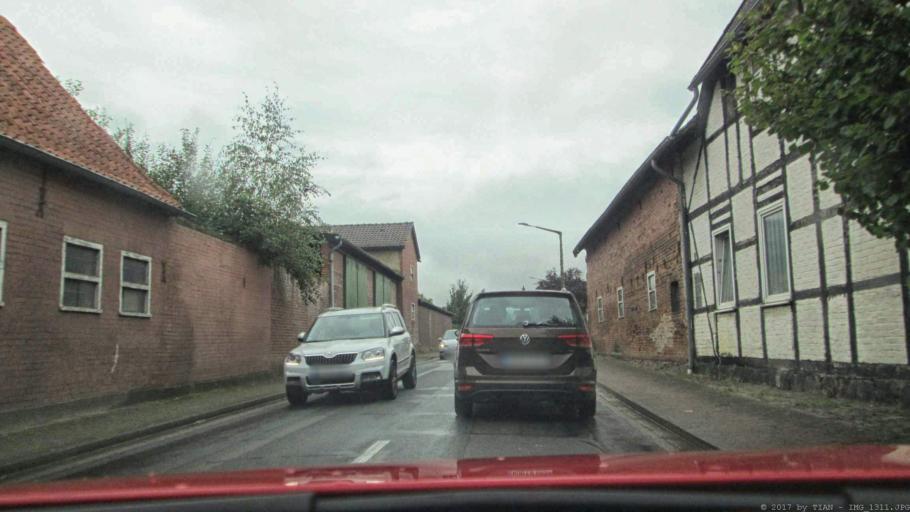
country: DE
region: Lower Saxony
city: Wittingen
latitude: 52.6991
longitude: 10.8083
